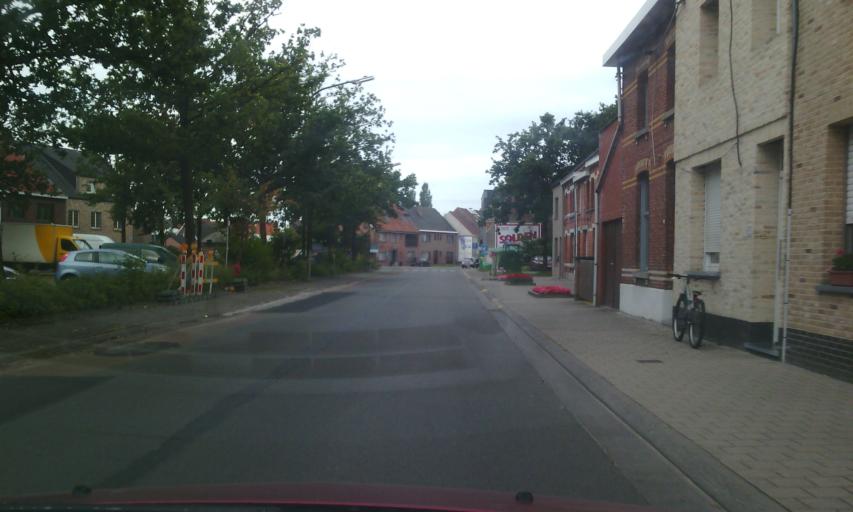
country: BE
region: Flanders
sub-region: Provincie Oost-Vlaanderen
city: Zele
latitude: 51.0699
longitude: 4.0339
